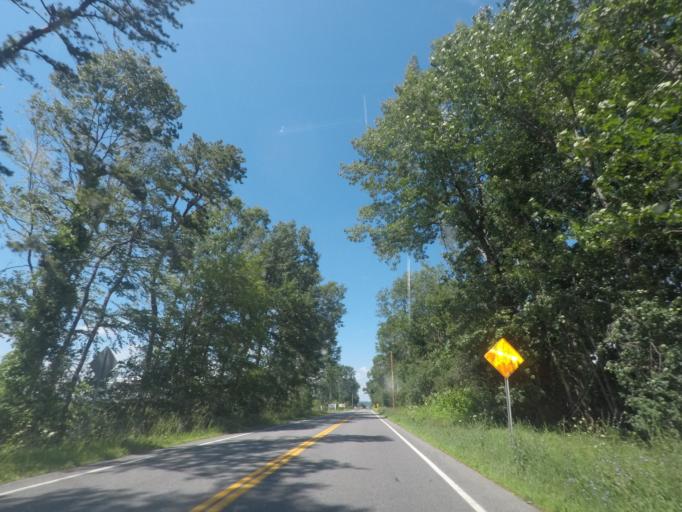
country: US
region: New York
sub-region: Schenectady County
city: Rotterdam
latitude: 42.7993
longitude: -73.9936
